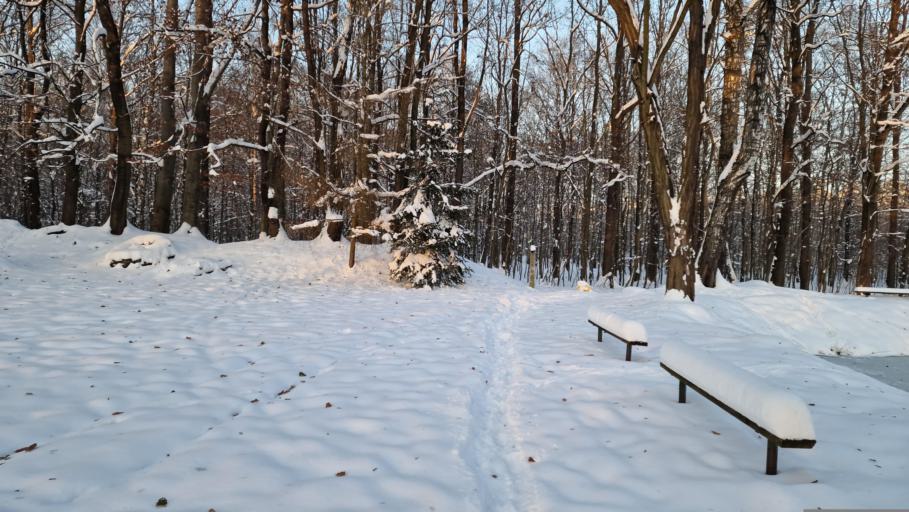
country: PL
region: Silesian Voivodeship
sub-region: Powiat gliwicki
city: Sosnicowice
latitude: 50.3064
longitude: 18.4904
